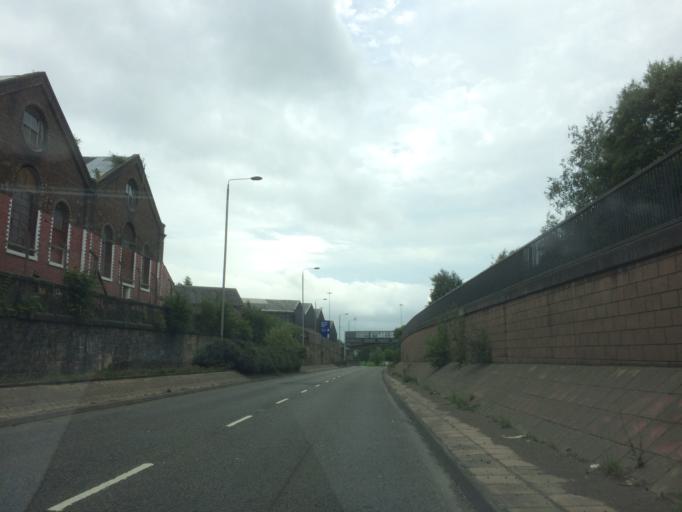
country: GB
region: Scotland
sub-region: Glasgow City
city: Glasgow
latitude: 55.8719
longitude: -4.2335
